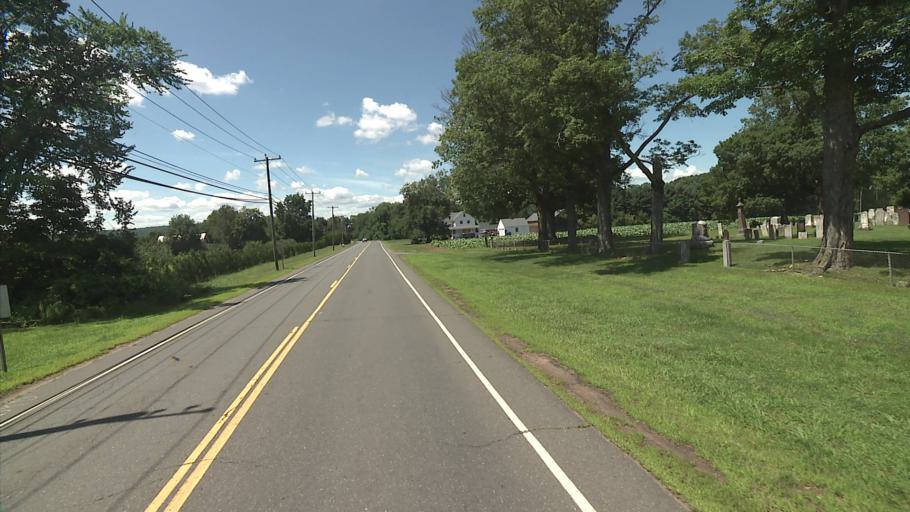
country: US
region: Connecticut
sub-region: Hartford County
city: Suffield Depot
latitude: 41.9886
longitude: -72.6938
